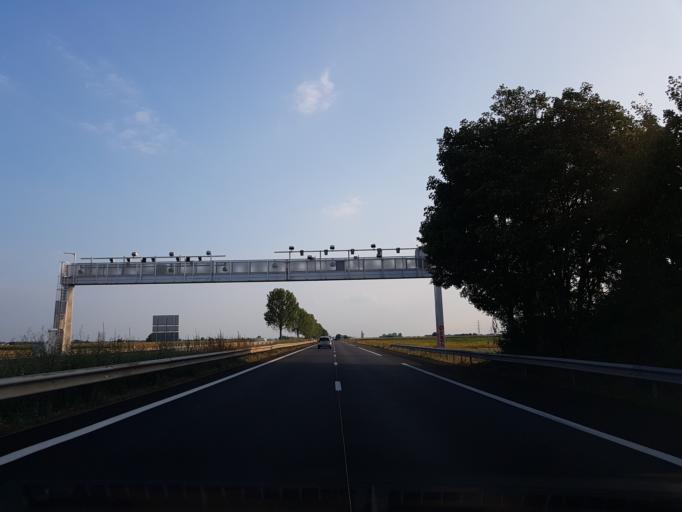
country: FR
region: Alsace
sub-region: Departement du Haut-Rhin
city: Oberhergheim
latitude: 47.9709
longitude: 7.3717
